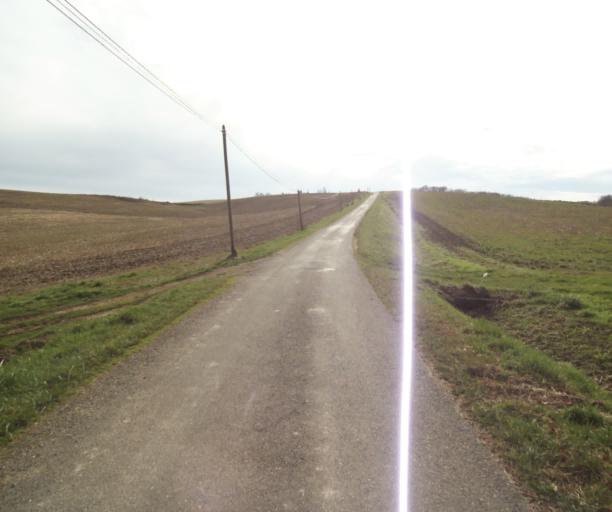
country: FR
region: Aquitaine
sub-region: Departement des Landes
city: Gabarret
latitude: 43.9417
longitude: 0.0463
